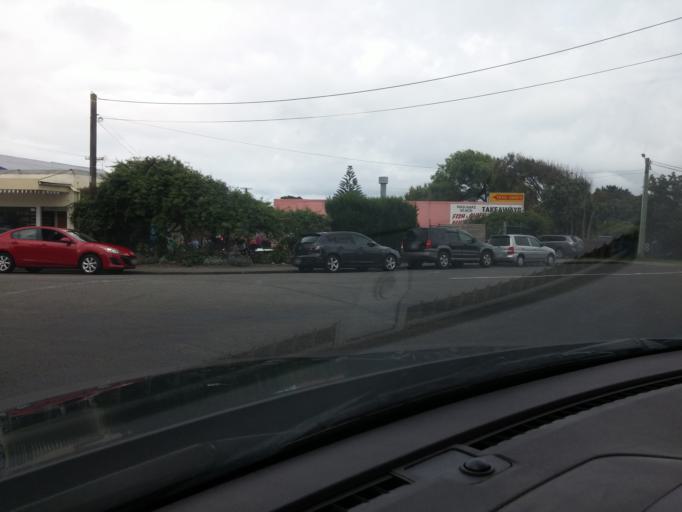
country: NZ
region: Wellington
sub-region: Kapiti Coast District
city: Paraparaumu
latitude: -40.8655
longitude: 175.0265
